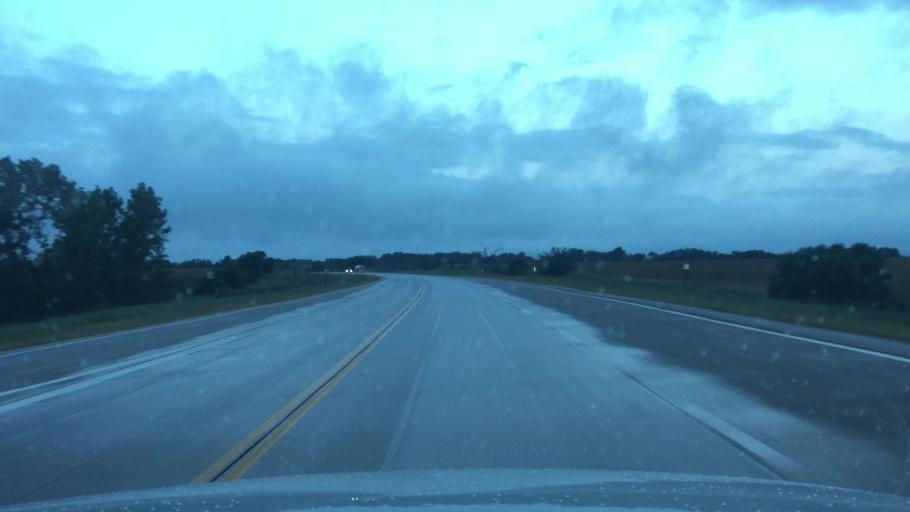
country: US
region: Kansas
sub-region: Neosho County
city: Chanute
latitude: 37.7234
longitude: -95.4744
